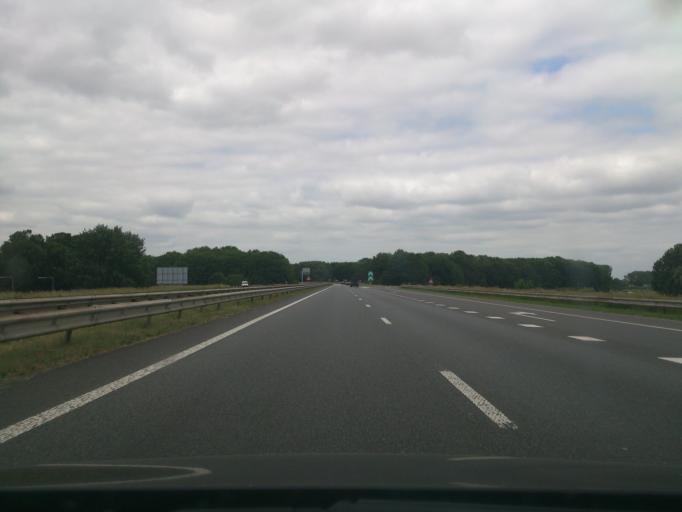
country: NL
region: Gelderland
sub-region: Gemeente Wijchen
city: Wijchen
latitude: 51.8142
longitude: 5.6859
